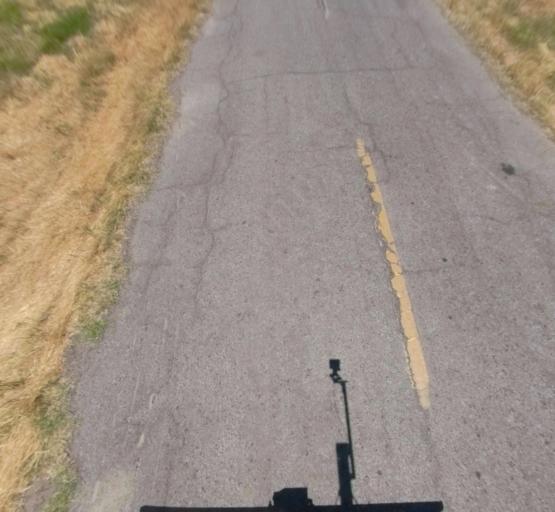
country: US
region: California
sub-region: Madera County
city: Chowchilla
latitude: 37.0544
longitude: -120.3363
